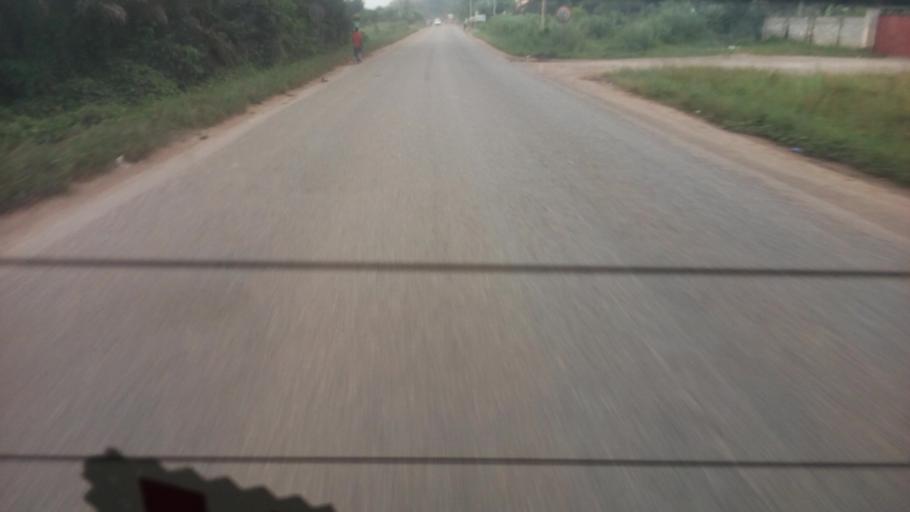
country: GH
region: Western
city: Tarkwa
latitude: 5.2122
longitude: -2.0267
